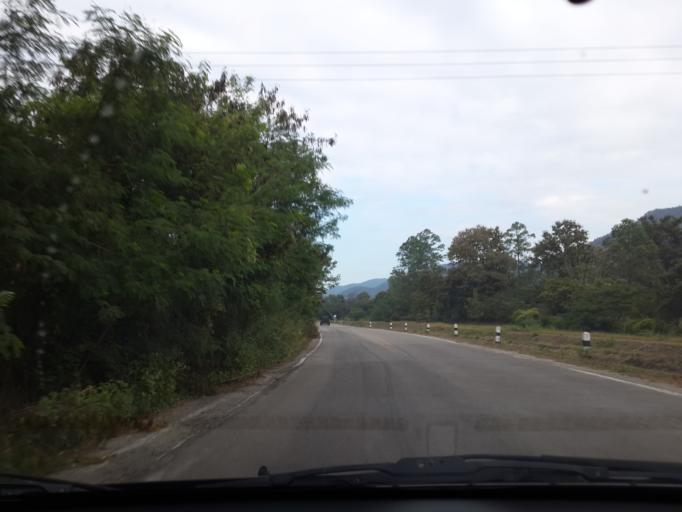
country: TH
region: Chiang Mai
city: San Sai
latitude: 18.9138
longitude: 99.1489
